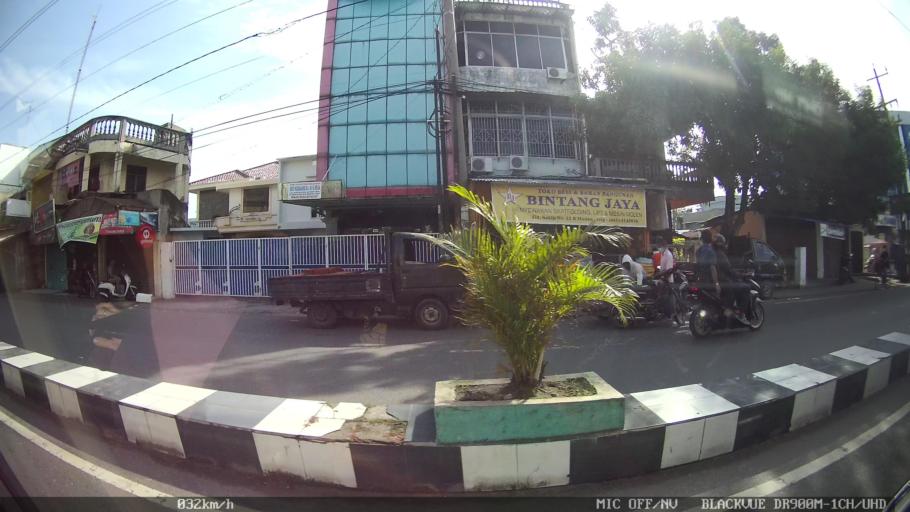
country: ID
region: North Sumatra
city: Medan
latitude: 3.5981
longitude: 98.6641
